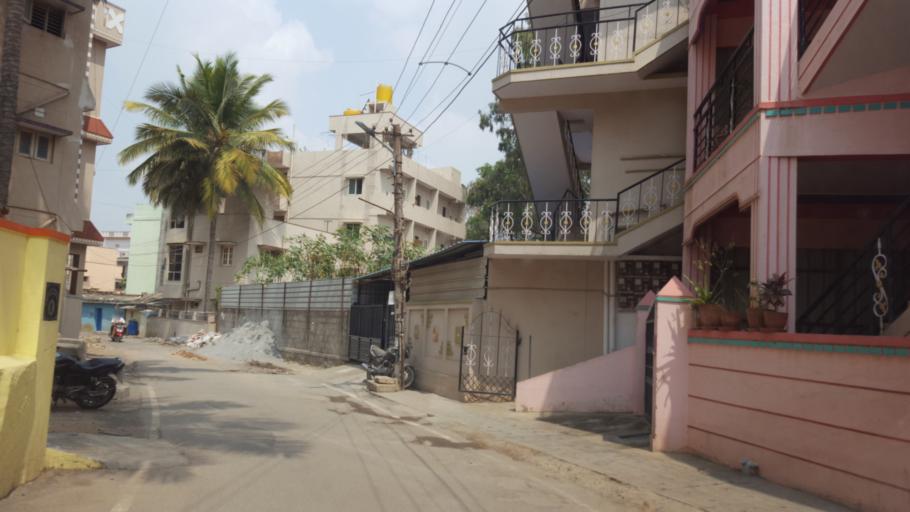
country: IN
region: Karnataka
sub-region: Bangalore Urban
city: Bangalore
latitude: 12.9884
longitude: 77.6862
